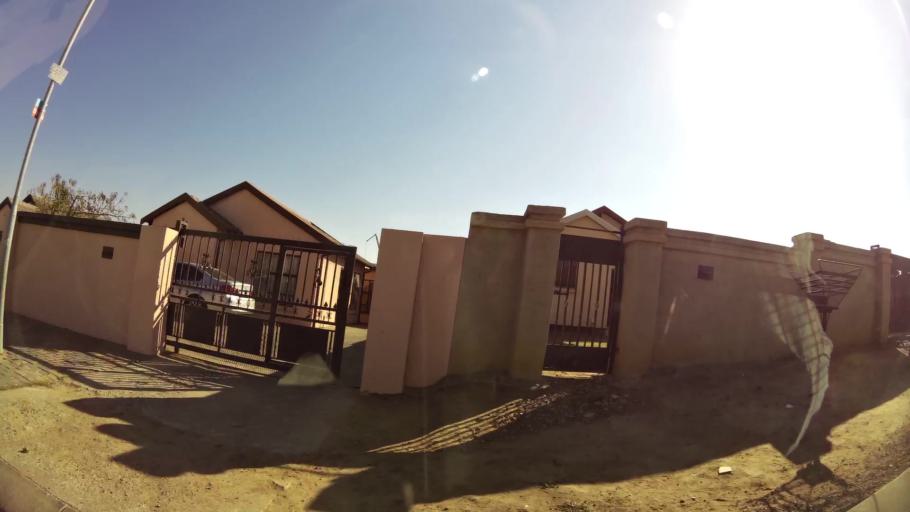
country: ZA
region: Gauteng
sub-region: City of Johannesburg Metropolitan Municipality
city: Modderfontein
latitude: -26.0445
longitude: 28.1970
